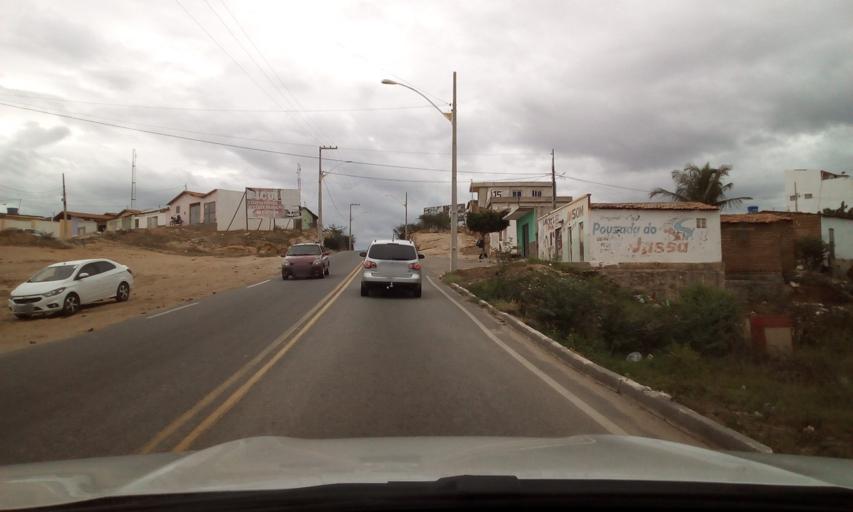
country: BR
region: Paraiba
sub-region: Picui
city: Picui
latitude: -6.5112
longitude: -36.3387
